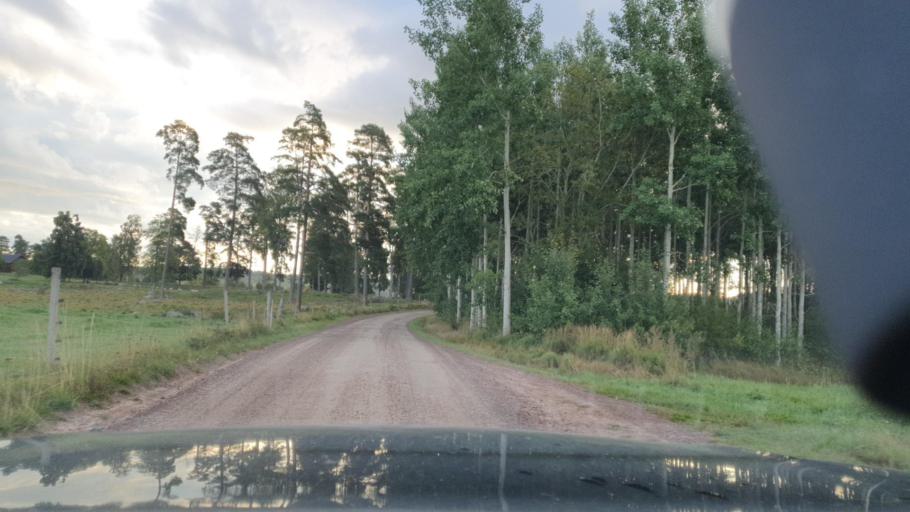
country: SE
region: Vaermland
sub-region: Kristinehamns Kommun
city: Kristinehamn
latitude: 59.3856
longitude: 14.0375
